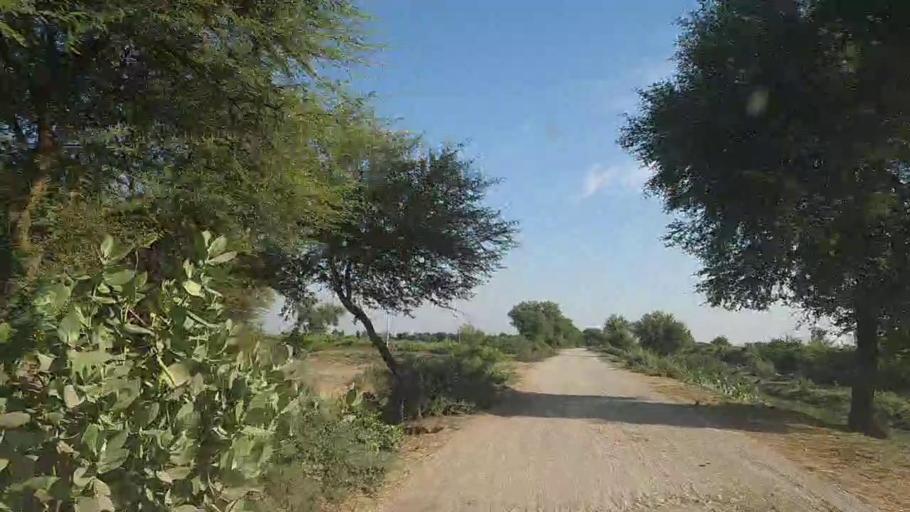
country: PK
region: Sindh
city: Bulri
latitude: 24.7808
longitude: 68.3537
